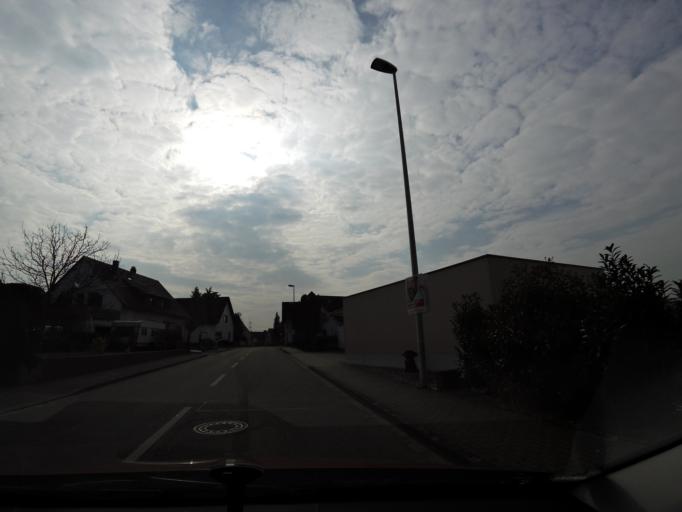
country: DE
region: Baden-Wuerttemberg
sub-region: Freiburg Region
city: Kehl
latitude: 48.5903
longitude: 7.8664
